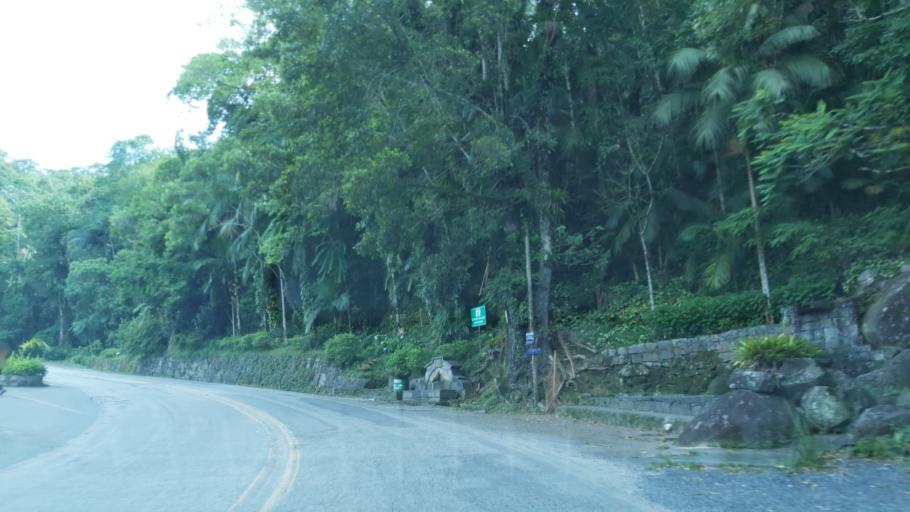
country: BR
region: Sao Paulo
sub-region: Miracatu
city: Miracatu
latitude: -24.0593
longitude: -47.5736
